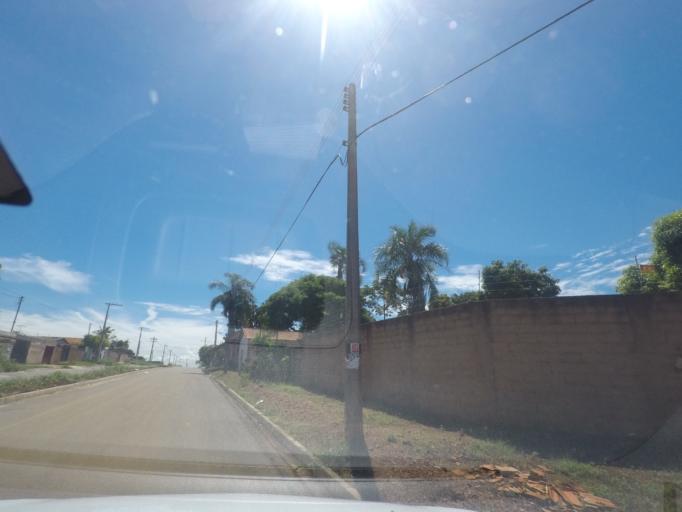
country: BR
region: Goias
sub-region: Aparecida De Goiania
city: Aparecida de Goiania
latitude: -16.7898
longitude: -49.3327
